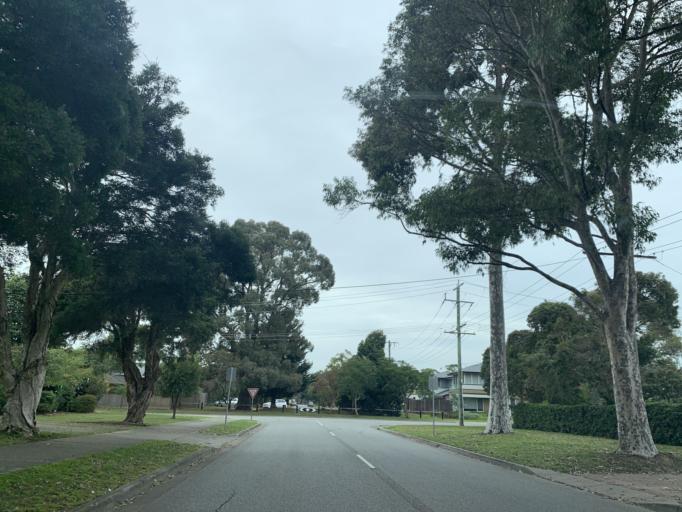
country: AU
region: Victoria
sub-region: Casey
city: Berwick
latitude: -38.0354
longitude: 145.3637
